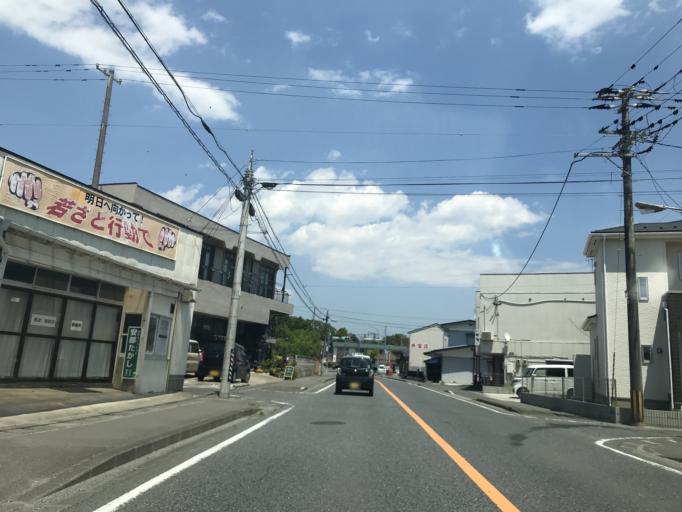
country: JP
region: Miyagi
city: Matsushima
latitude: 38.3797
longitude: 141.0787
